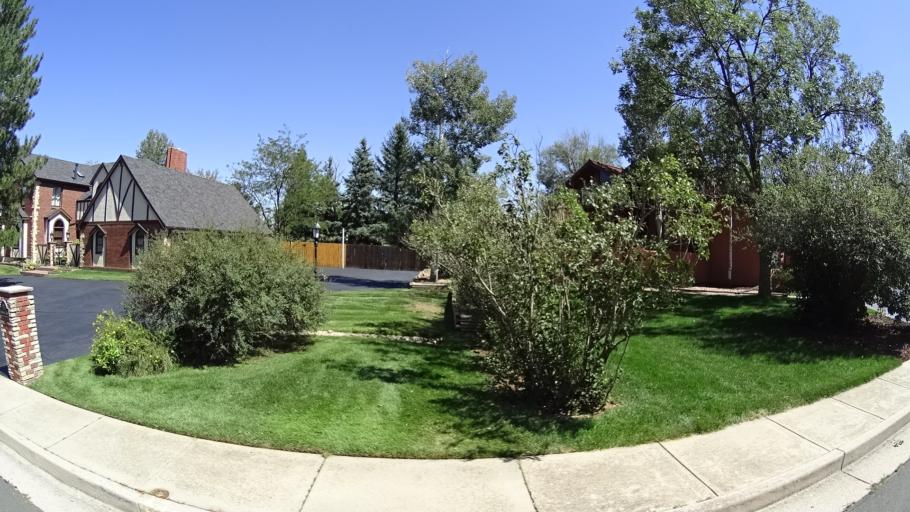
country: US
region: Colorado
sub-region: El Paso County
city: Colorado Springs
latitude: 38.7875
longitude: -104.8361
